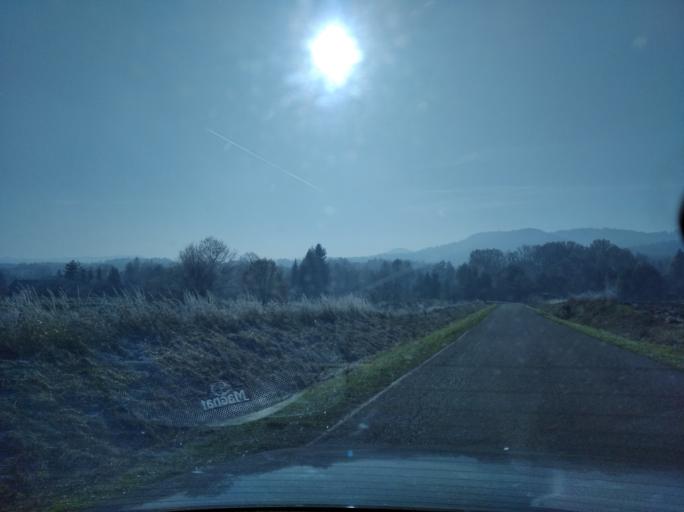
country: PL
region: Subcarpathian Voivodeship
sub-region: Powiat strzyzowski
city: Wysoka Strzyzowska
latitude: 49.8364
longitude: 21.7132
